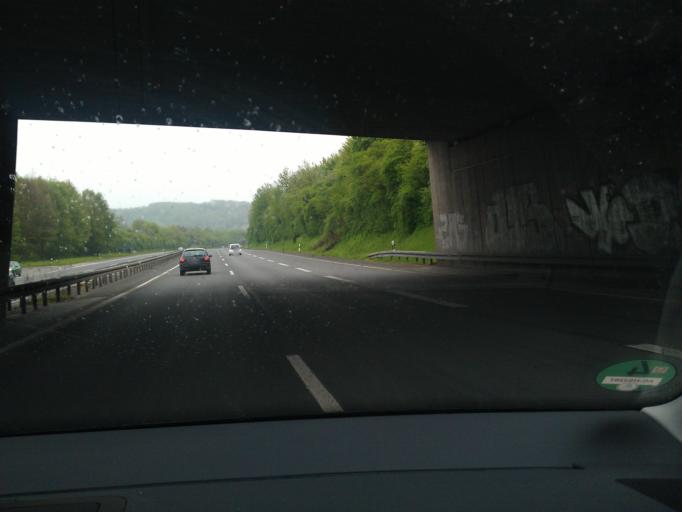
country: DE
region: North Rhine-Westphalia
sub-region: Regierungsbezirk Koln
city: Hennef
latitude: 50.7810
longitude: 7.2685
